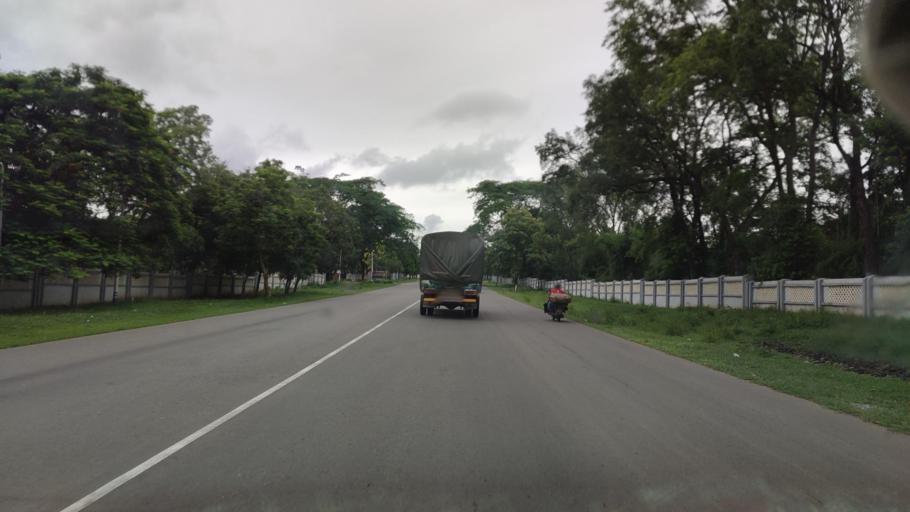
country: MM
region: Mandalay
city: Meiktila
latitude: 20.8493
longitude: 95.8870
